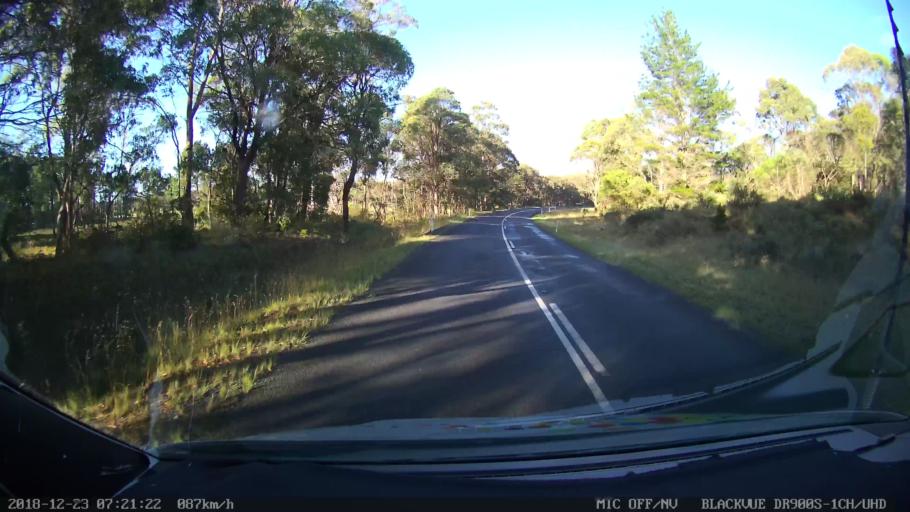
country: AU
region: New South Wales
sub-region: Bellingen
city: Dorrigo
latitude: -30.4971
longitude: 152.2643
